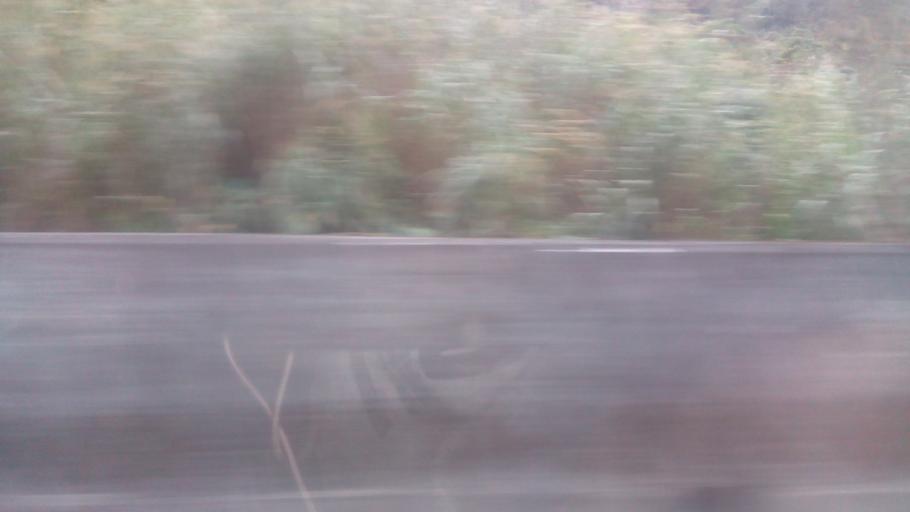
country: TW
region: Taiwan
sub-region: Yilan
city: Yilan
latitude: 24.5755
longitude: 121.4805
